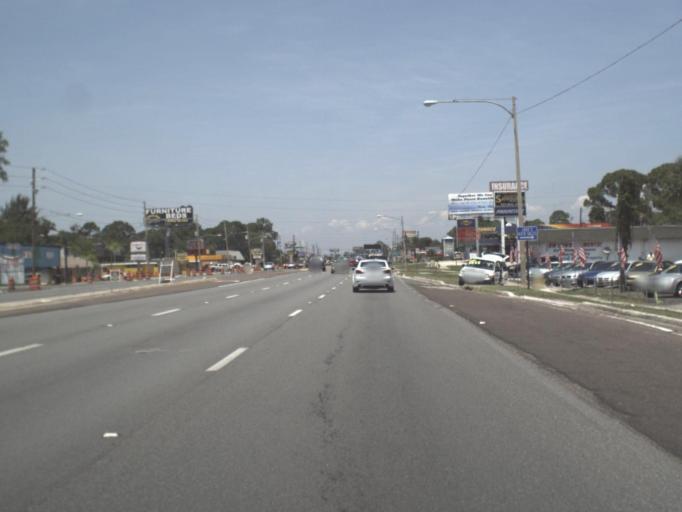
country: US
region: Florida
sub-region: Pasco County
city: Port Richey
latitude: 28.2742
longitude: -82.7219
